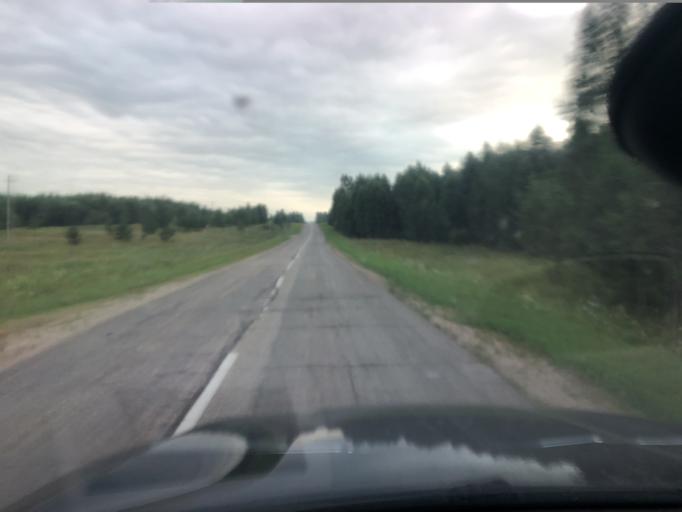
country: RU
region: Jaroslavl
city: Petrovsk
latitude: 57.0097
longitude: 39.0060
